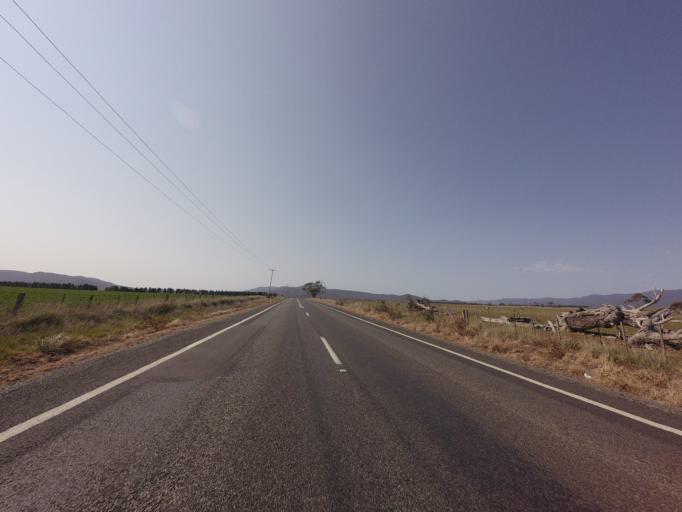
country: AU
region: Tasmania
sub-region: Northern Midlands
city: Evandale
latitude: -41.8018
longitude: 147.6891
